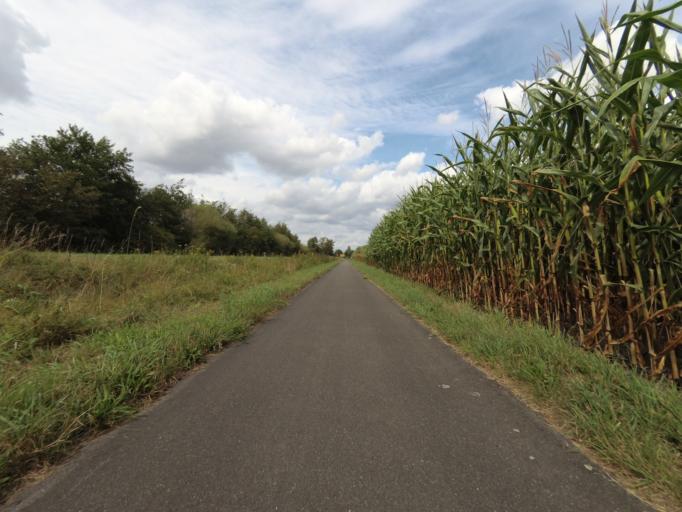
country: DE
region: North Rhine-Westphalia
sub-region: Regierungsbezirk Munster
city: Gronau
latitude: 52.1745
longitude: 6.9750
